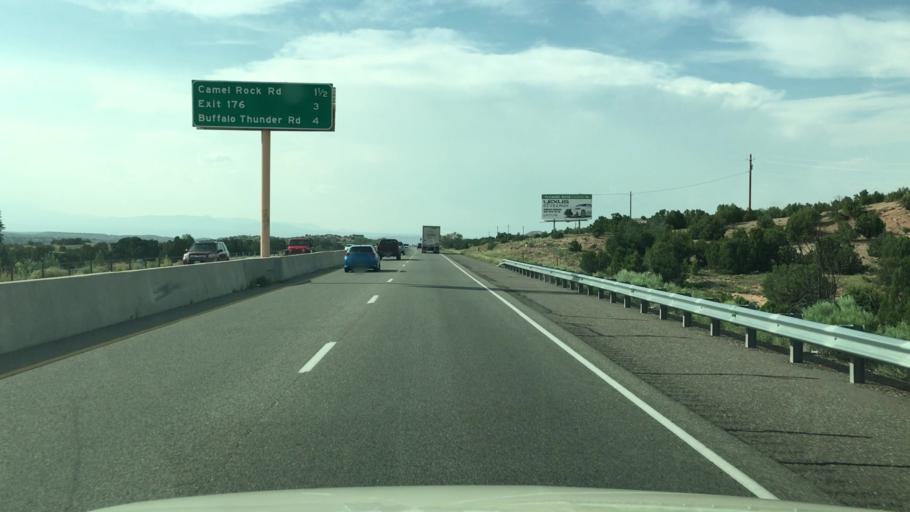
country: US
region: New Mexico
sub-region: Santa Fe County
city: Nambe
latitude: 35.8010
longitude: -105.9601
